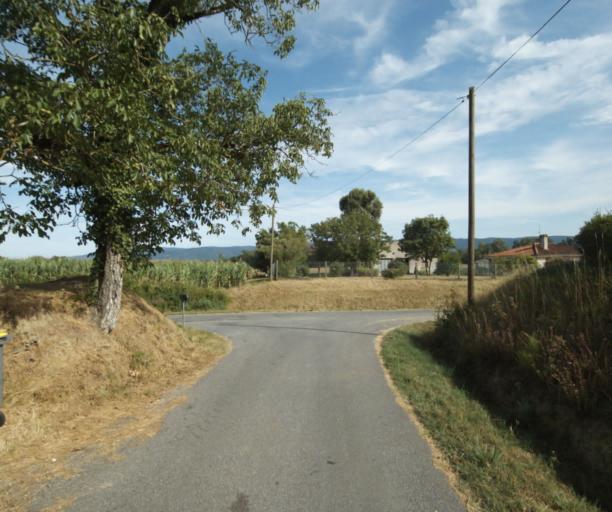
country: FR
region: Midi-Pyrenees
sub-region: Departement du Tarn
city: Soual
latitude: 43.5315
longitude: 2.0792
